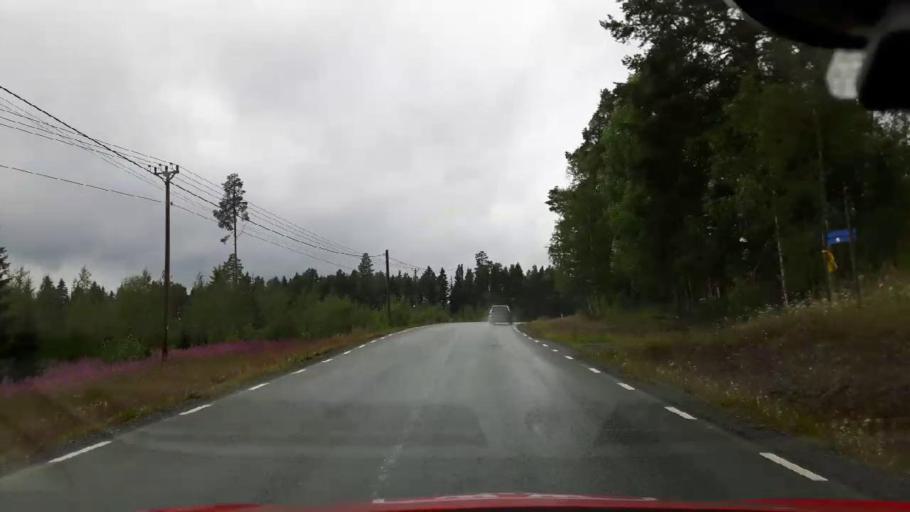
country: SE
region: Jaemtland
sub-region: Krokoms Kommun
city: Krokom
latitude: 63.3500
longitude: 14.1841
